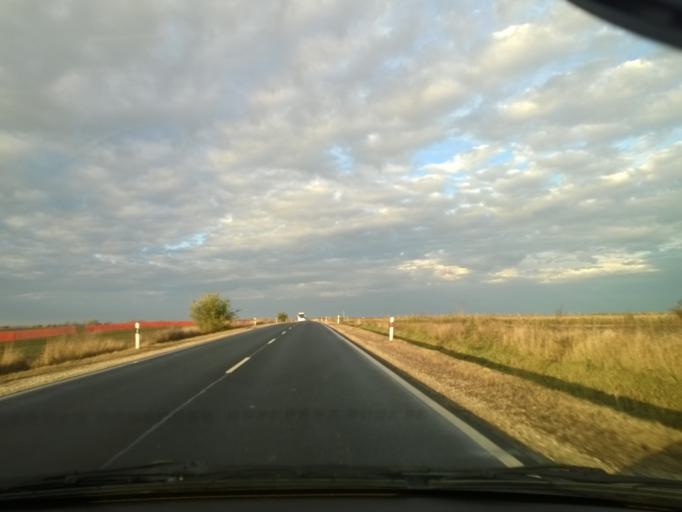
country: HU
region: Bacs-Kiskun
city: Kalocsa
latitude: 46.5824
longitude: 18.9760
